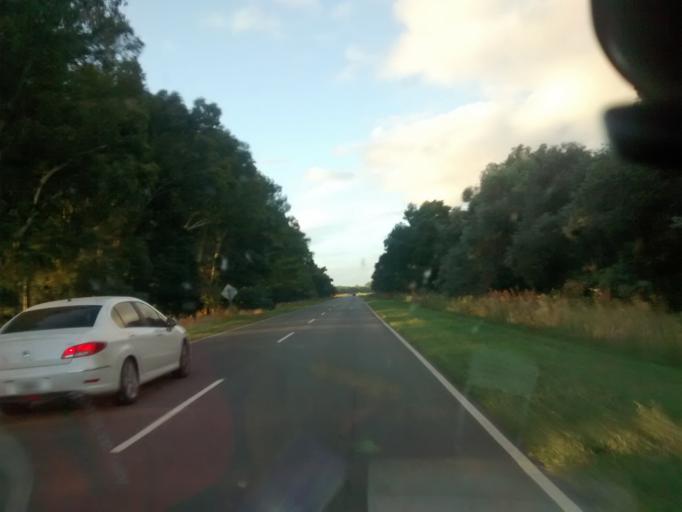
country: AR
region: Buenos Aires
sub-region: Partido de General Belgrano
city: General Belgrano
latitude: -35.6552
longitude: -58.4726
